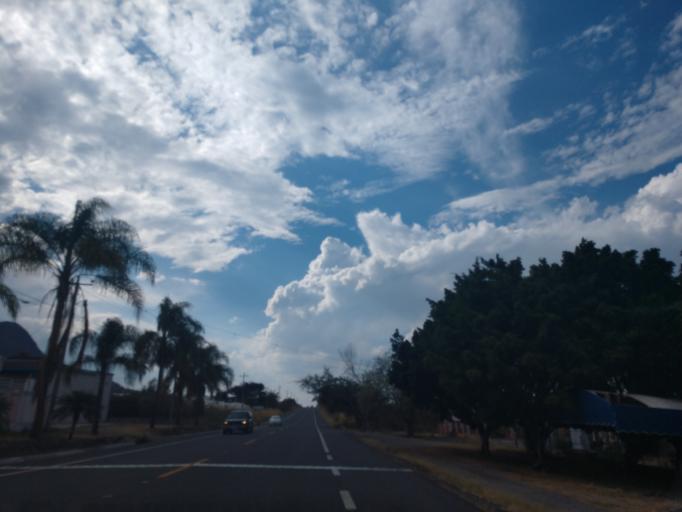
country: MX
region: Jalisco
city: Chapala
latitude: 20.1719
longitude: -103.2175
